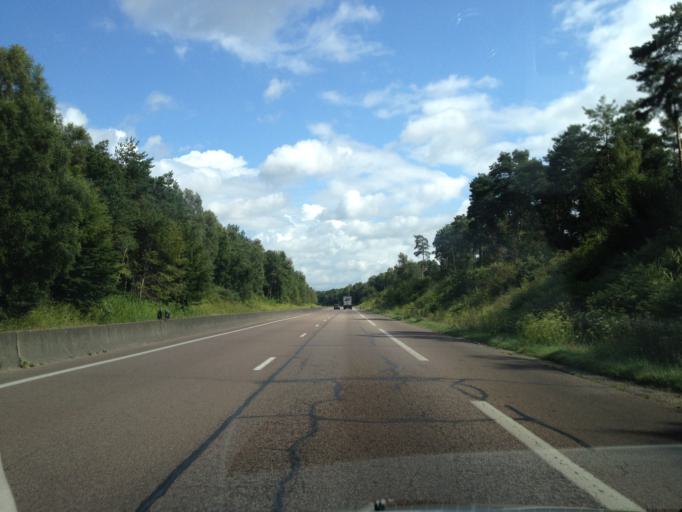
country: FR
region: Haute-Normandie
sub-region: Departement de la Seine-Maritime
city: Oissel
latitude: 49.3531
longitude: 1.0815
